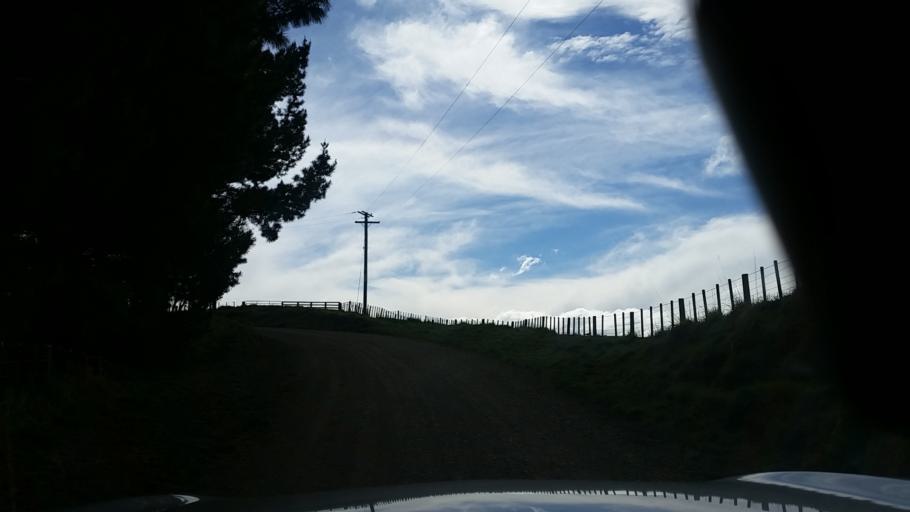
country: NZ
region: Hawke's Bay
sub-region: Napier City
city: Napier
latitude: -39.2164
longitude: 176.9826
